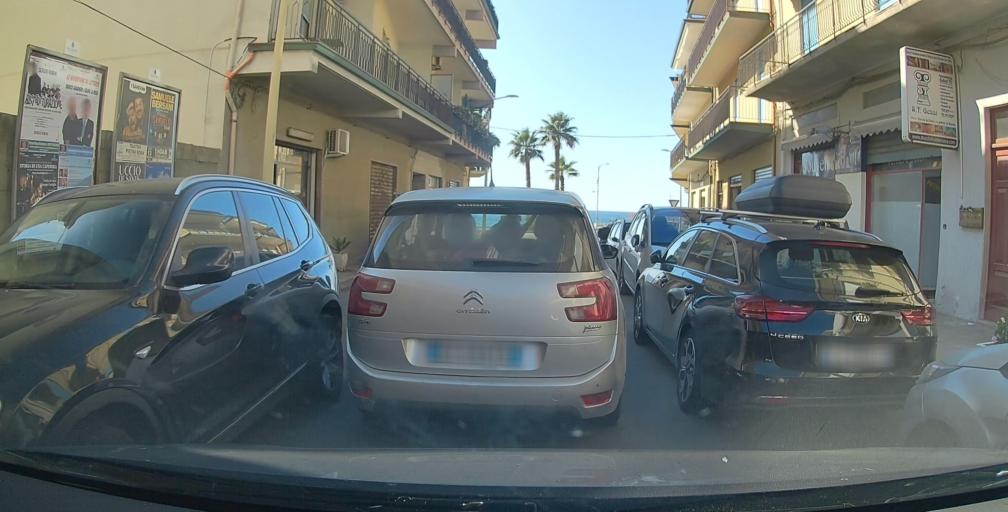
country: IT
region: Sicily
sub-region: Messina
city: Capo d'Orlando
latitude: 38.1636
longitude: 14.7472
